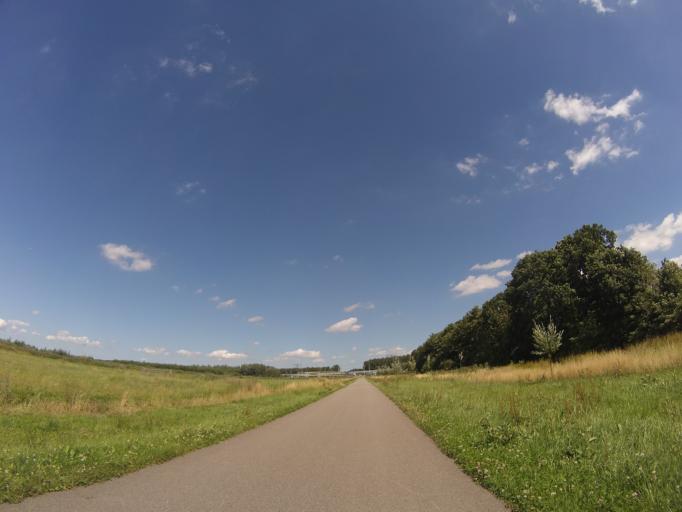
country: NL
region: Utrecht
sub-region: Stichtse Vecht
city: Spechtenkamp
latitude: 52.1338
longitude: 5.0046
